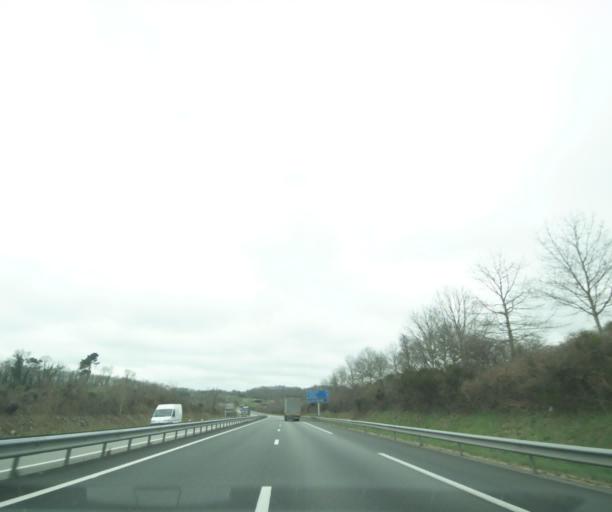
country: FR
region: Limousin
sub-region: Departement de la Haute-Vienne
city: Saint-Sulpice-les-Feuilles
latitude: 46.3446
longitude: 1.4223
